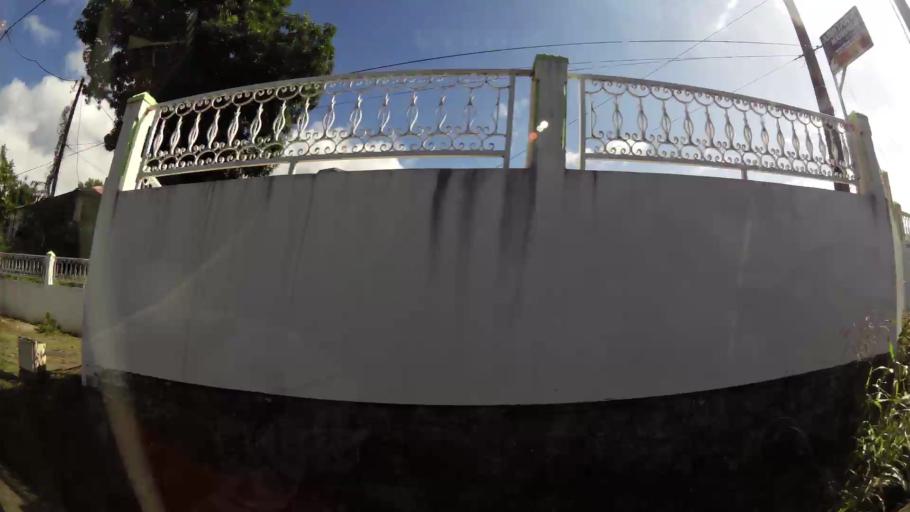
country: GP
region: Guadeloupe
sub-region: Guadeloupe
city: Bouillante
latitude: 16.0946
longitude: -61.7689
